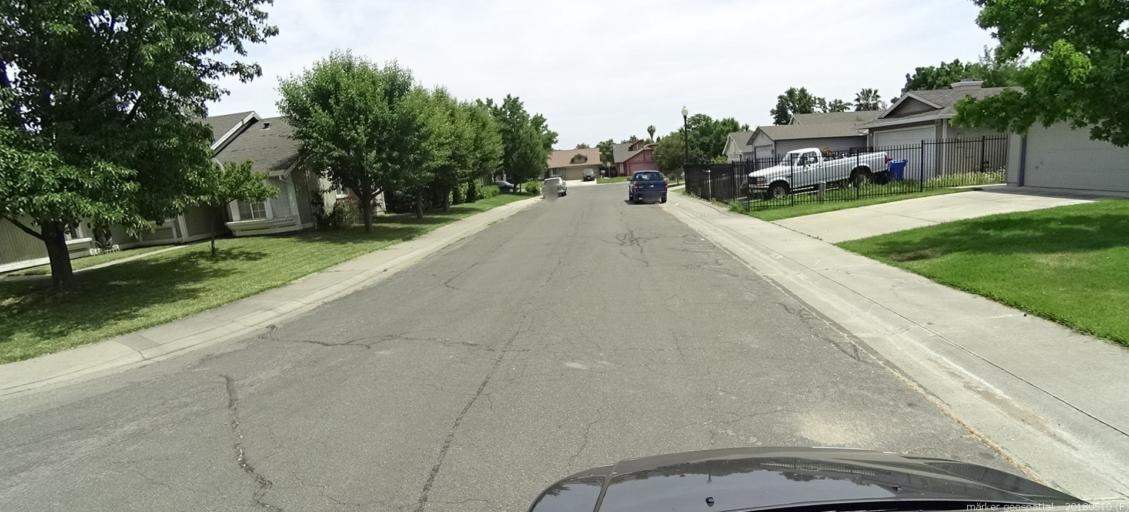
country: US
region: California
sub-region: Sacramento County
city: Rio Linda
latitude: 38.6576
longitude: -121.4645
